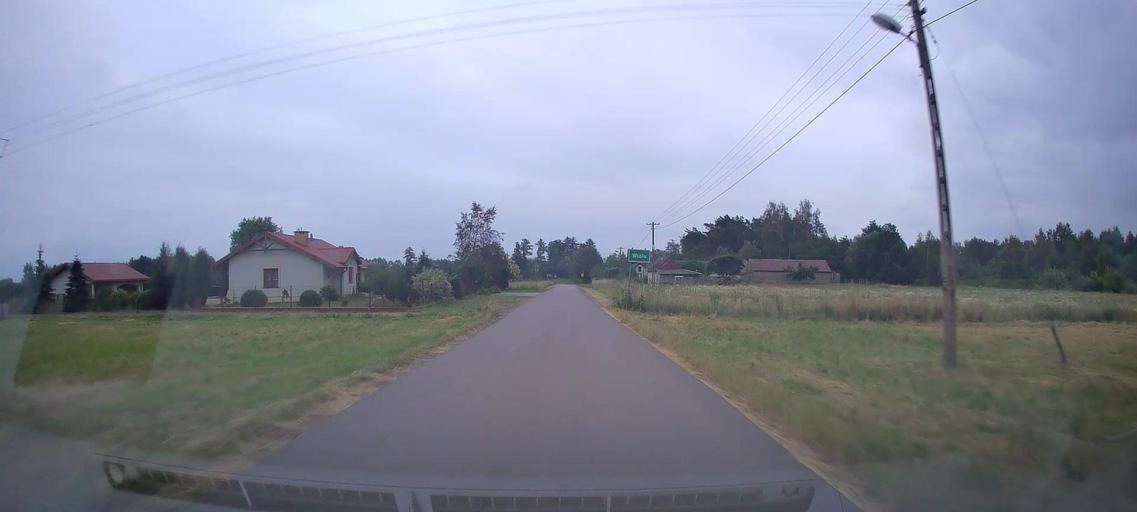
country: PL
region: Masovian Voivodeship
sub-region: Powiat radomski
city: Jedlinsk
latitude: 51.4730
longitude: 21.1146
